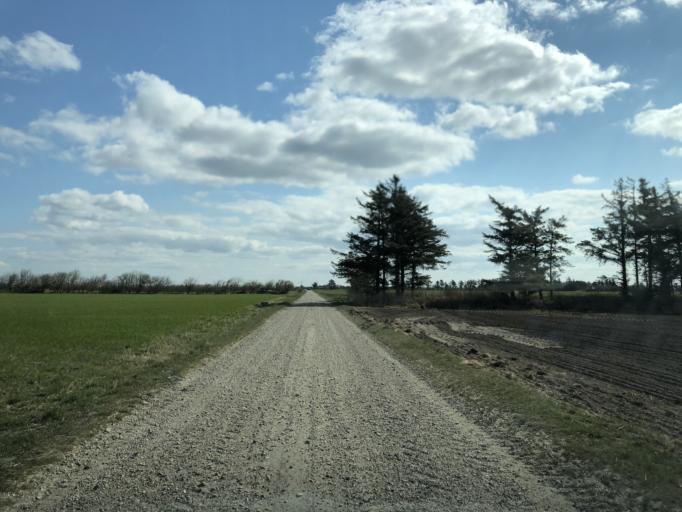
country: DK
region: Central Jutland
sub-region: Holstebro Kommune
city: Ulfborg
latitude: 56.4020
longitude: 8.1926
